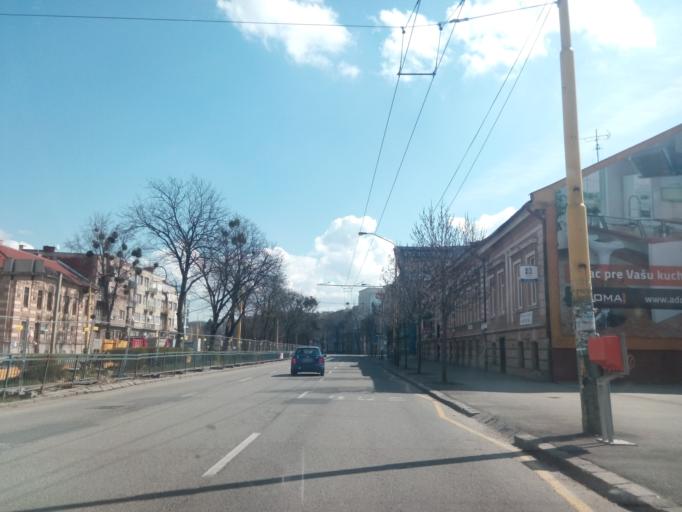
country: SK
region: Kosicky
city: Kosice
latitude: 48.7163
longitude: 21.2541
